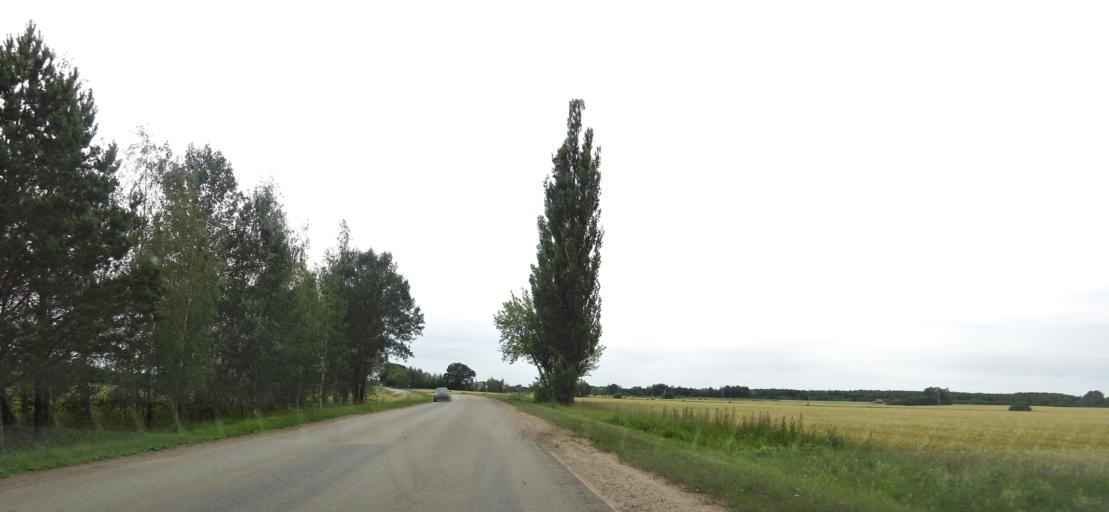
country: LT
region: Panevezys
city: Pasvalys
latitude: 56.0884
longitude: 24.4896
